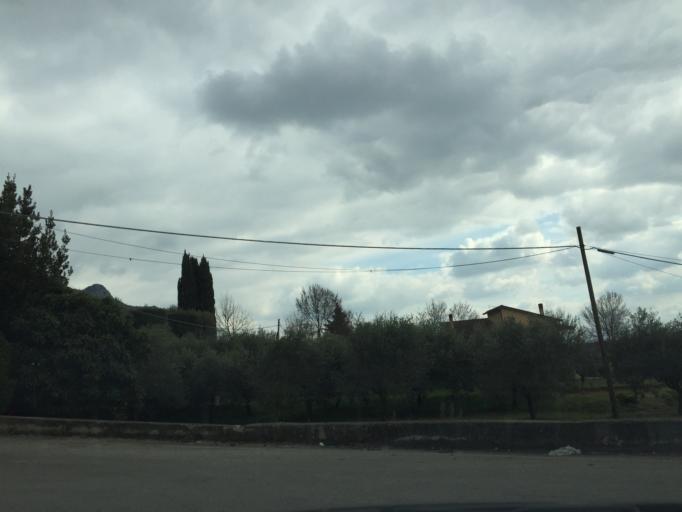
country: IT
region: Latium
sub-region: Provincia di Frosinone
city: Villa Santa Lucia
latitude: 41.4903
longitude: 13.7840
